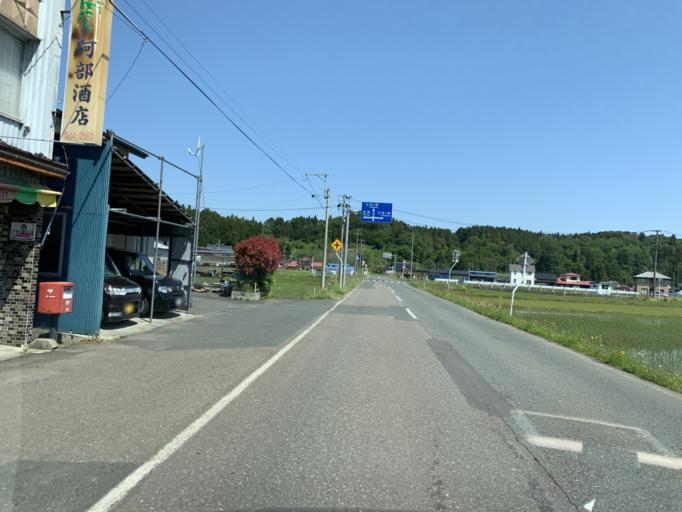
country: JP
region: Iwate
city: Mizusawa
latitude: 39.1568
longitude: 141.0649
